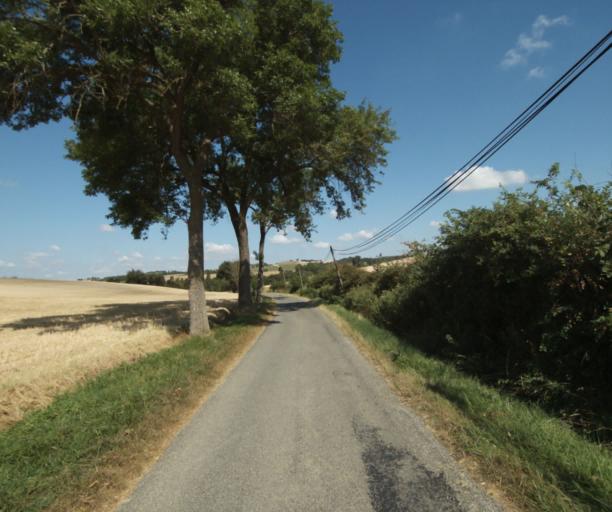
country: FR
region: Midi-Pyrenees
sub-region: Departement de la Haute-Garonne
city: Auriac-sur-Vendinelle
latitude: 43.4547
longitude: 1.7898
